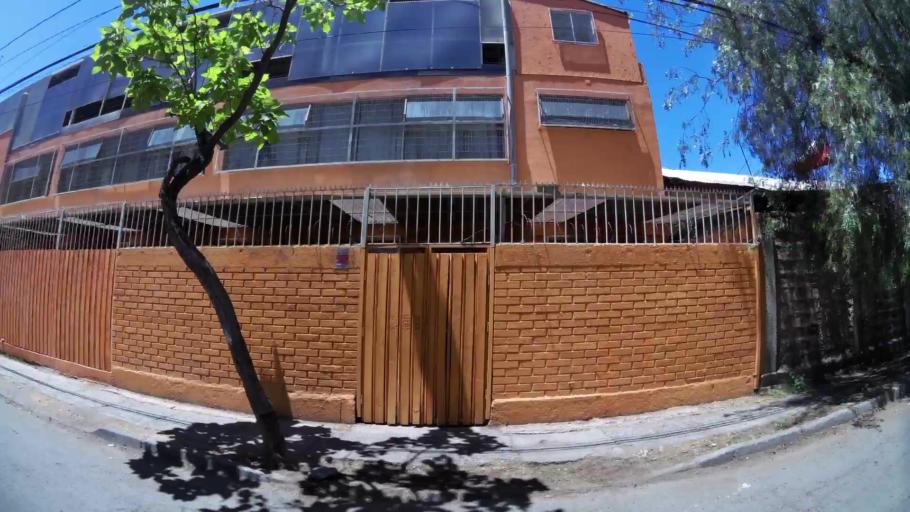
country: CL
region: Santiago Metropolitan
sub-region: Provincia de Maipo
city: San Bernardo
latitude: -33.5799
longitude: -70.6742
